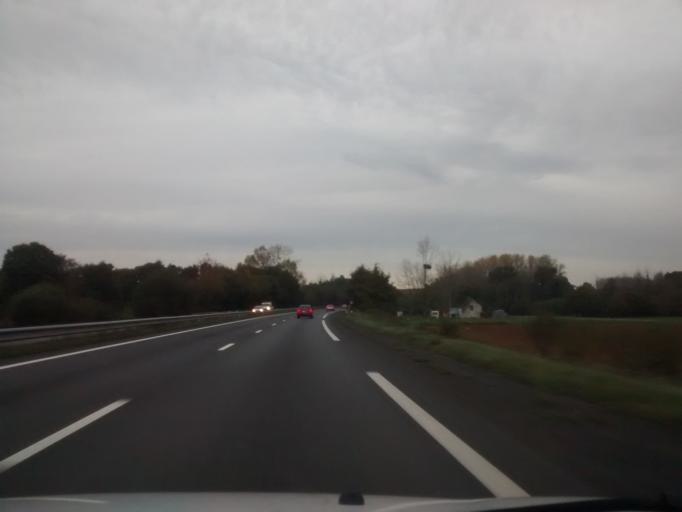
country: FR
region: Brittany
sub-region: Departement des Cotes-d'Armor
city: Broons
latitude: 48.2978
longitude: -2.2292
